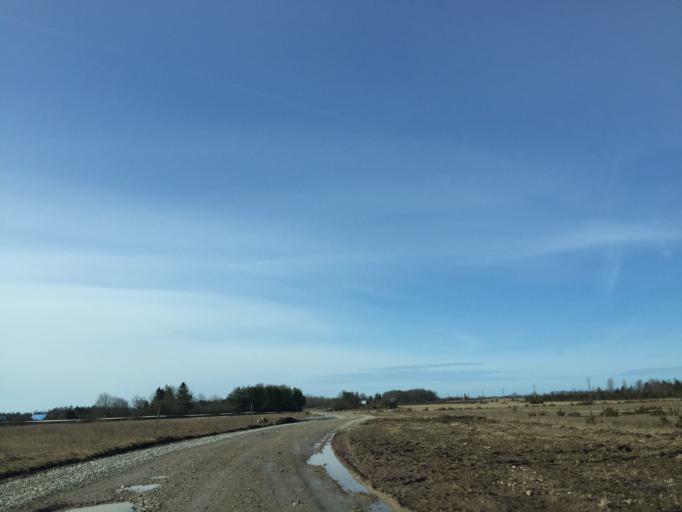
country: EE
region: Laeaene
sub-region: Haapsalu linn
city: Haapsalu
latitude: 58.6705
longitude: 23.5372
